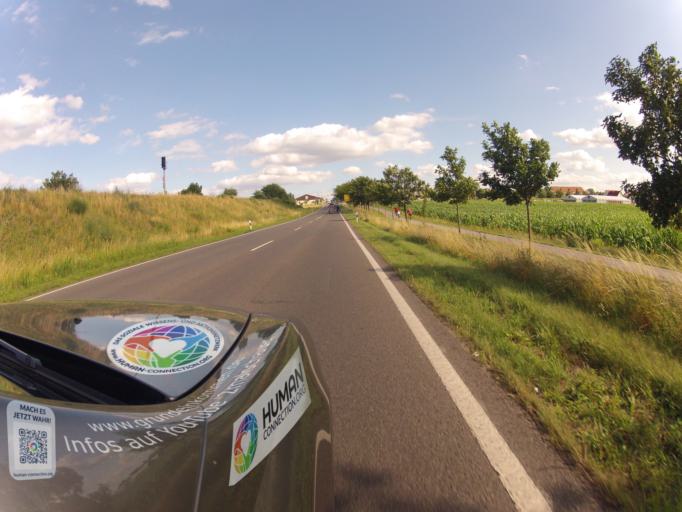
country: DE
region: Mecklenburg-Vorpommern
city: Loddin
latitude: 54.0170
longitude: 14.0444
